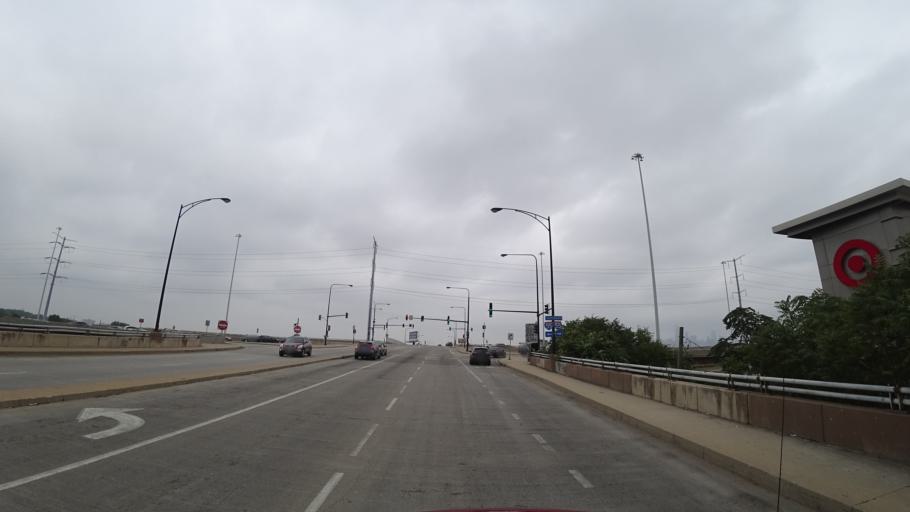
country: US
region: Illinois
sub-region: Cook County
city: Chicago
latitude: 41.8362
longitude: -87.6754
